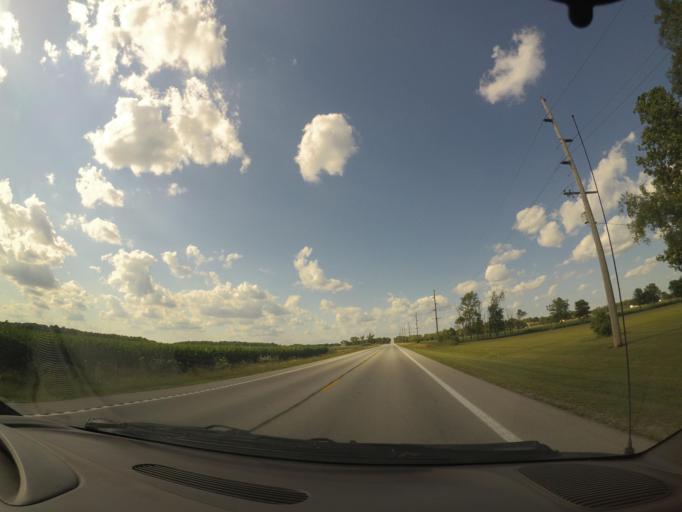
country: US
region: Ohio
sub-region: Wood County
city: Pemberville
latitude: 41.4022
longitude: -83.4159
